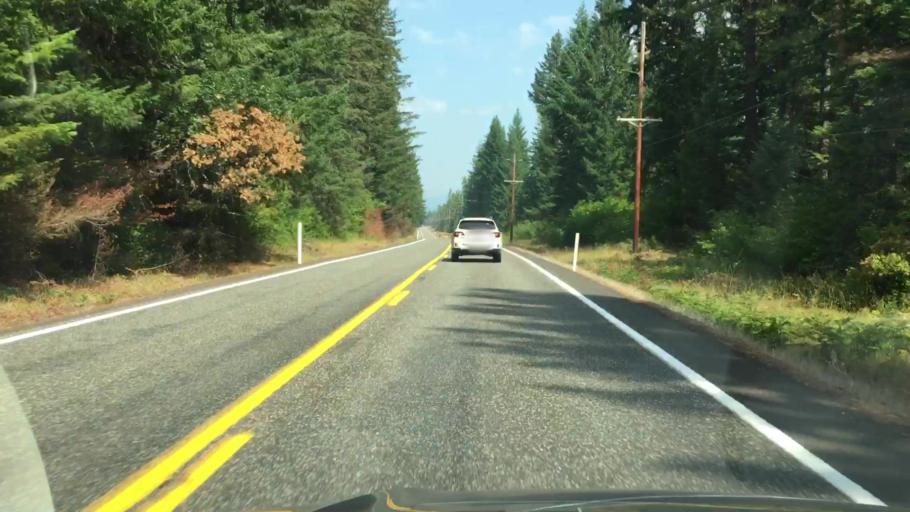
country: US
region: Washington
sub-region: Klickitat County
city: White Salmon
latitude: 45.9157
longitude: -121.4995
